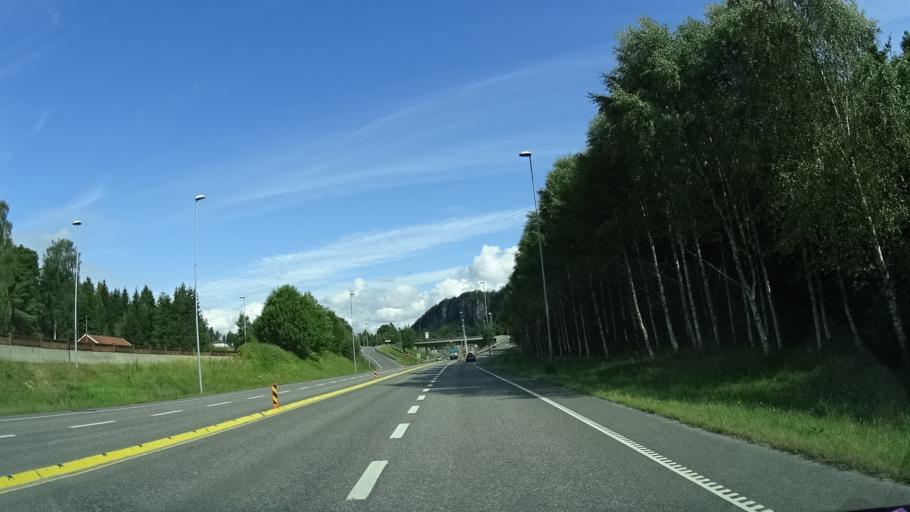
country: NO
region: Telemark
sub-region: Bamble
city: Langesund
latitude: 59.0335
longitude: 9.6772
